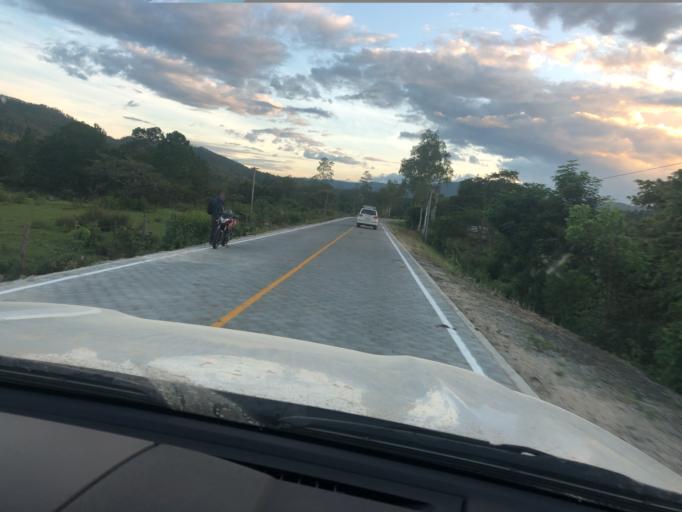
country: HN
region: El Paraiso
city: Santa Cruz
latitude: 13.7215
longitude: -86.6226
